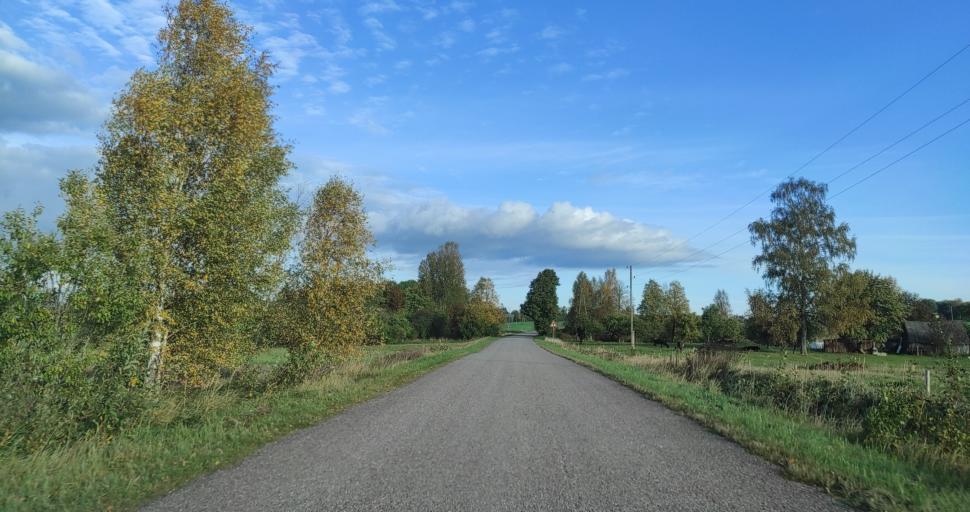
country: LV
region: Aizpute
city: Aizpute
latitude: 56.7571
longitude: 21.7820
